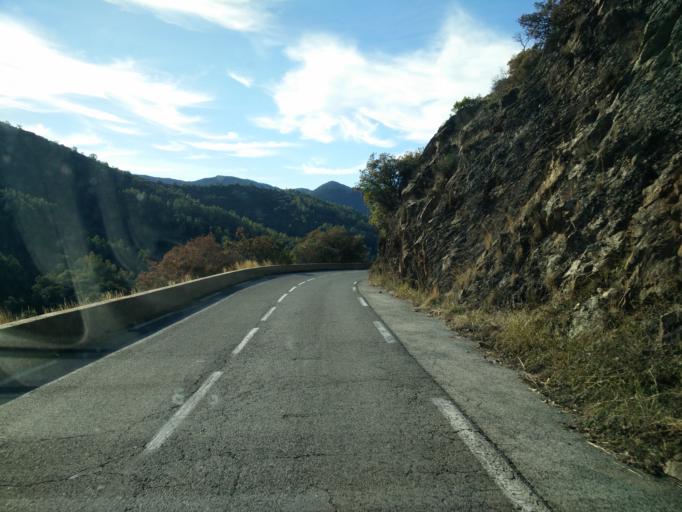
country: FR
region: Provence-Alpes-Cote d'Azur
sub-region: Departement du Var
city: La Garde-Freinet
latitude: 43.3314
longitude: 6.4520
